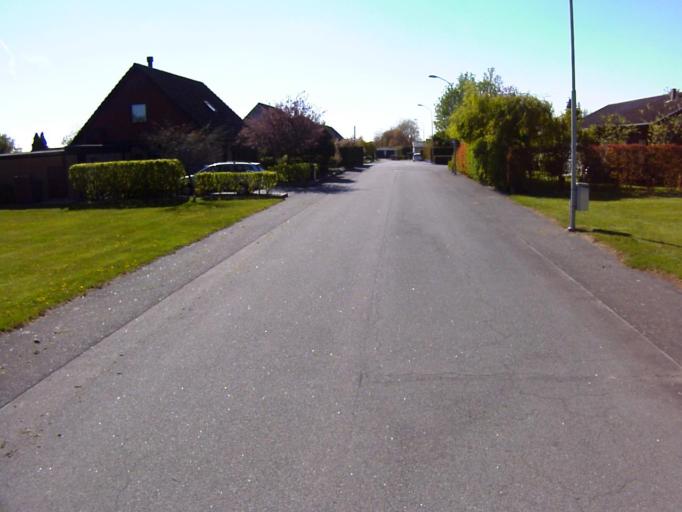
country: SE
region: Skane
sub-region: Kristianstads Kommun
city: Kristianstad
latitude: 56.0314
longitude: 14.2056
